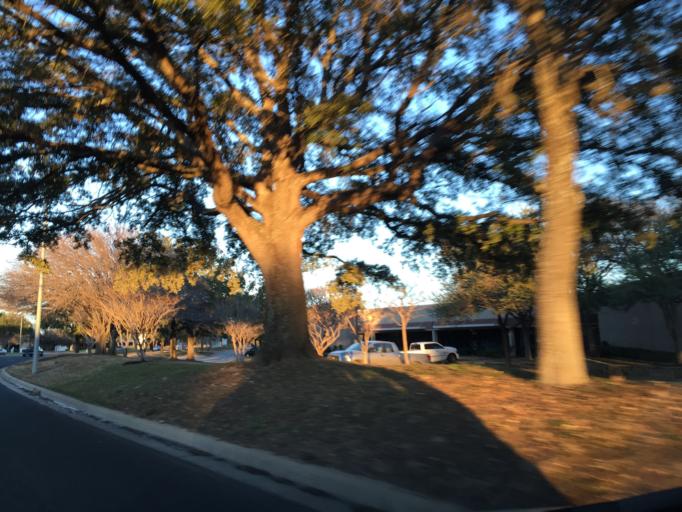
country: US
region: Texas
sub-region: Travis County
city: Wells Branch
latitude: 30.3921
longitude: -97.7126
